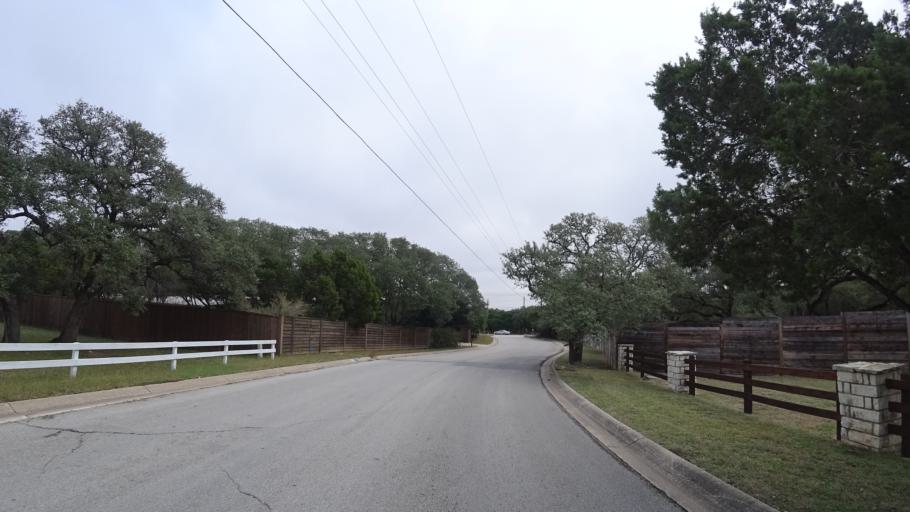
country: US
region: Texas
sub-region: Travis County
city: Shady Hollow
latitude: 30.2213
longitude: -97.8942
